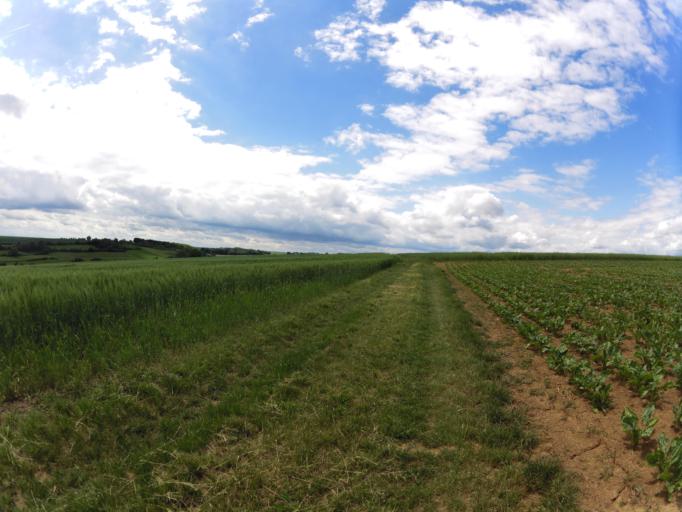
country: DE
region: Bavaria
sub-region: Regierungsbezirk Unterfranken
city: Winterhausen
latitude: 49.6705
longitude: 10.0093
